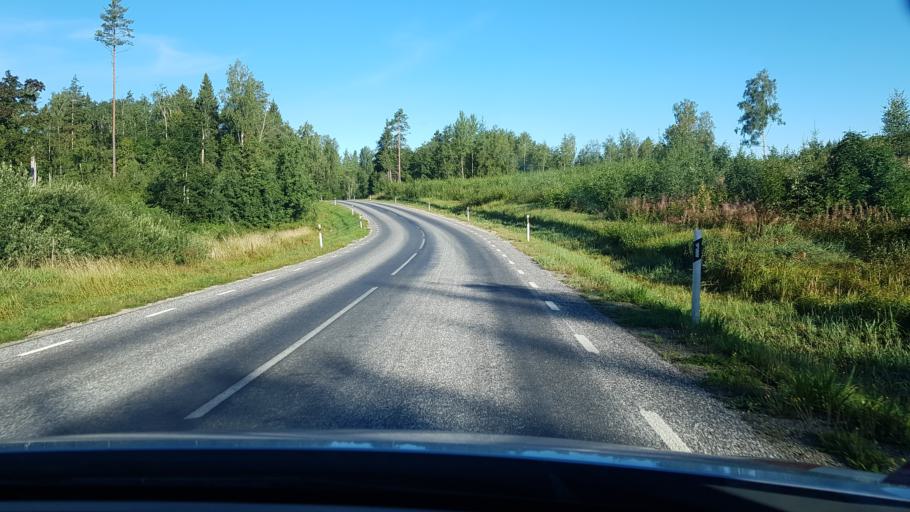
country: EE
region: Vorumaa
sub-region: Antsla vald
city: Vana-Antsla
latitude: 58.0156
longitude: 26.5922
